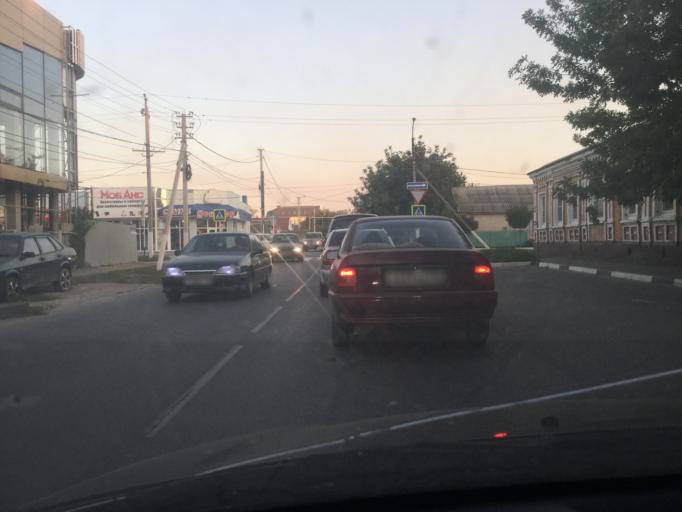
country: RU
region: Krasnodarskiy
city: Slavyansk-na-Kubani
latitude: 45.2562
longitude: 38.1224
